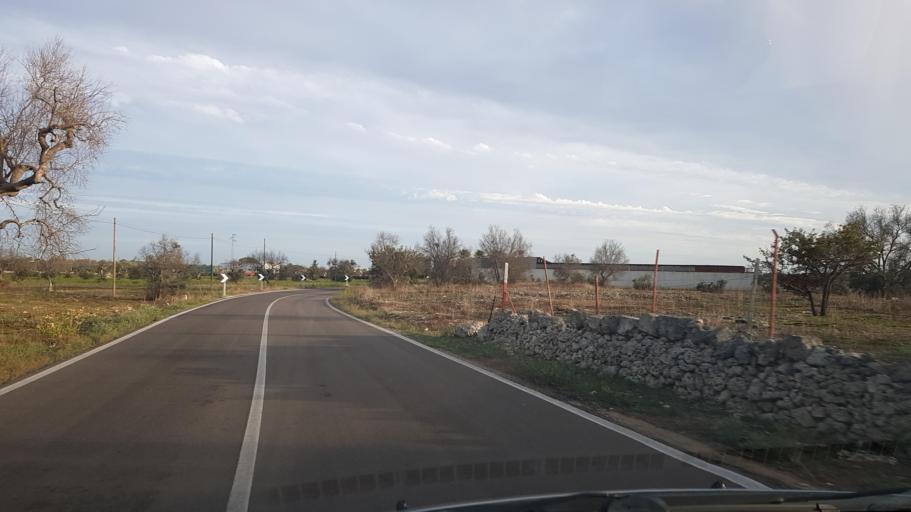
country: IT
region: Apulia
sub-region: Provincia di Lecce
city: Surbo
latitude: 40.4160
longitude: 18.1229
